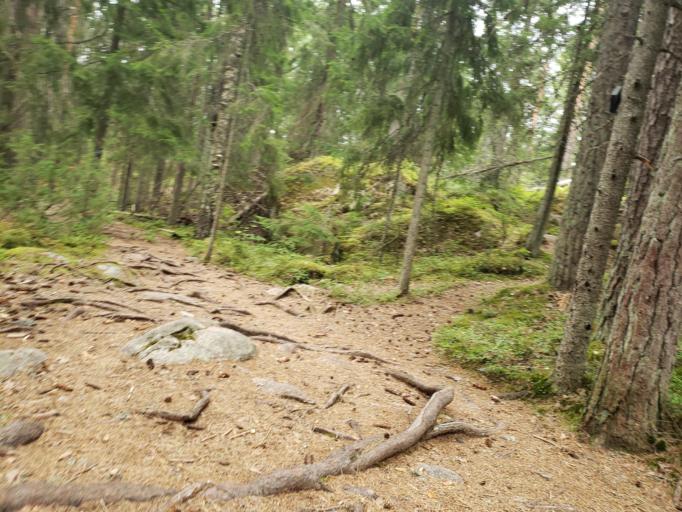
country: FI
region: Uusimaa
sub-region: Helsinki
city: Espoo
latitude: 60.3102
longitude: 24.5016
